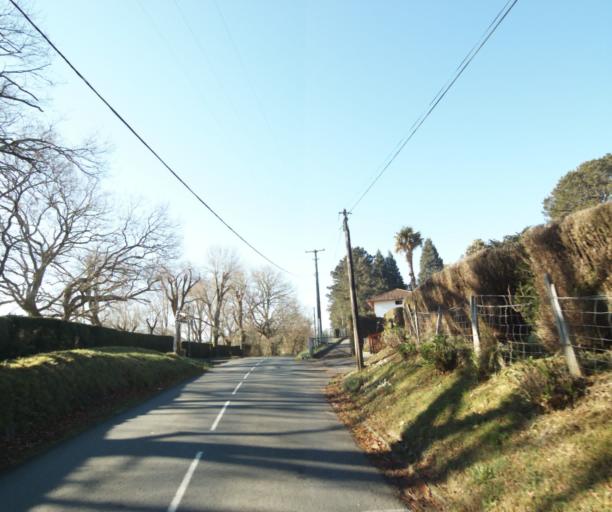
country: FR
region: Aquitaine
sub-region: Departement des Pyrenees-Atlantiques
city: Ciboure
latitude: 43.3549
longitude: -1.6660
